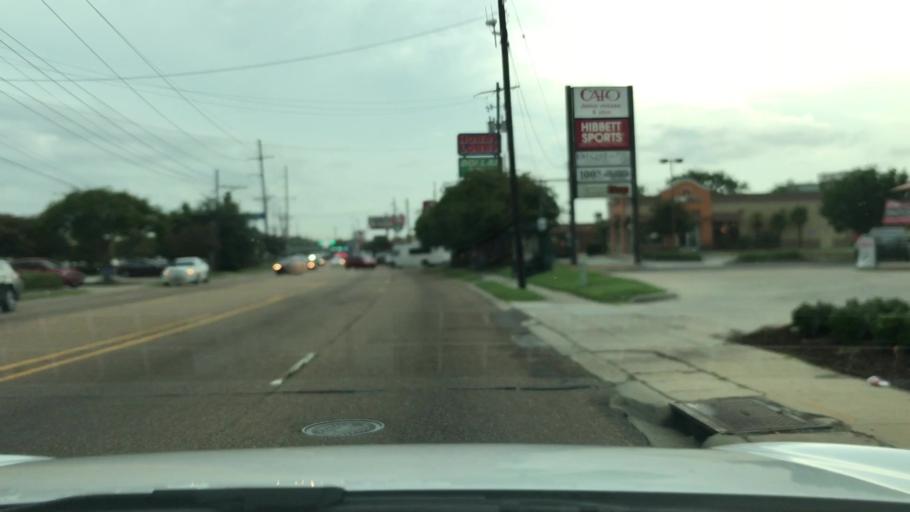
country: US
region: Louisiana
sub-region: East Baton Rouge Parish
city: Baton Rouge
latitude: 30.4187
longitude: -91.1417
